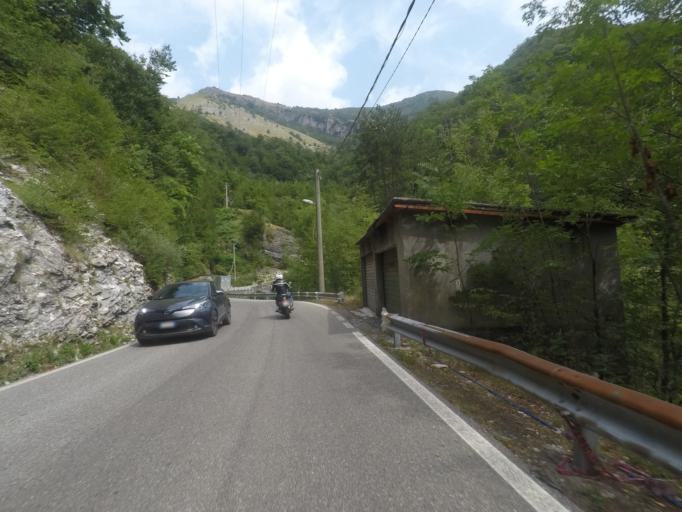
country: IT
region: Tuscany
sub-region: Provincia di Lucca
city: Careggine
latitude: 44.0656
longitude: 10.3116
